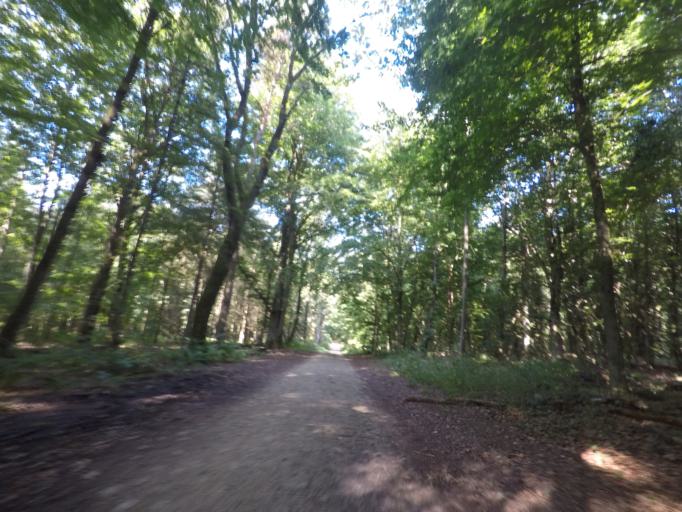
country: LU
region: Luxembourg
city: Itzig
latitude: 49.6089
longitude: 6.1801
